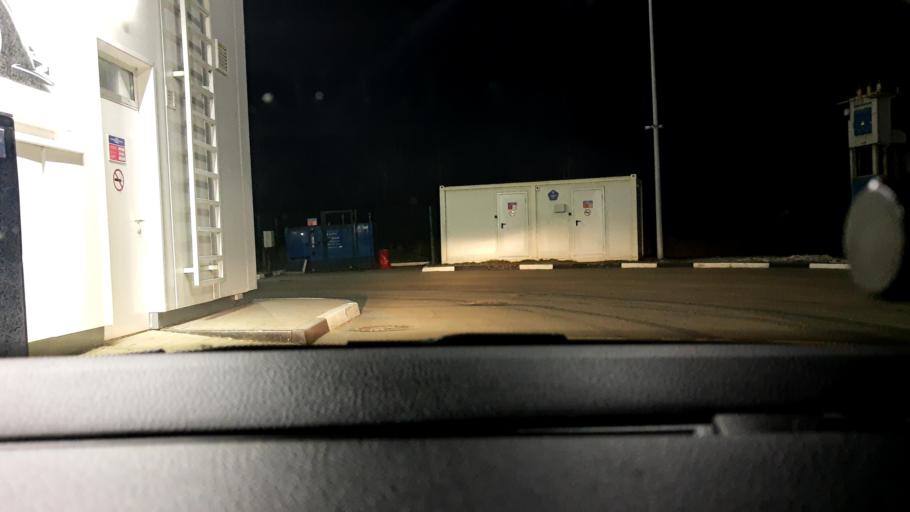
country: RU
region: Vladimir
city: Vorsha
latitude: 56.0842
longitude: 40.2079
